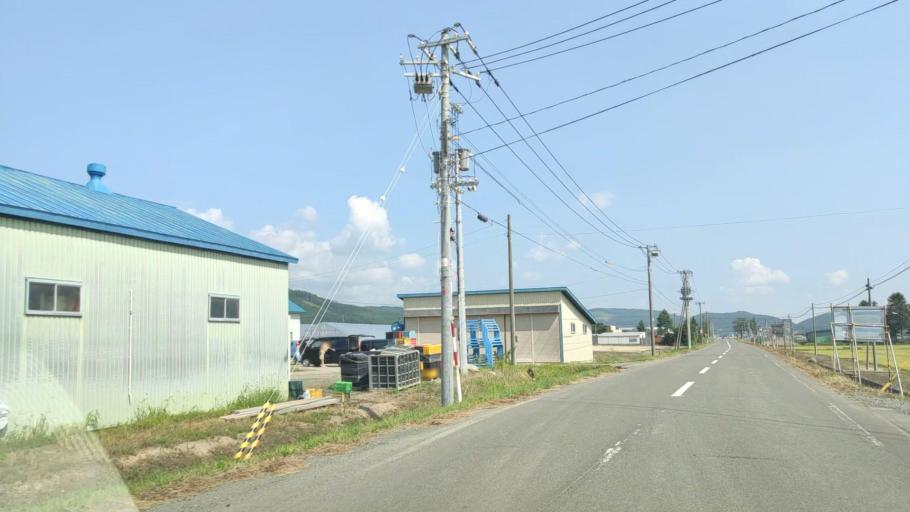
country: JP
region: Hokkaido
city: Shimo-furano
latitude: 43.3881
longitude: 142.3938
